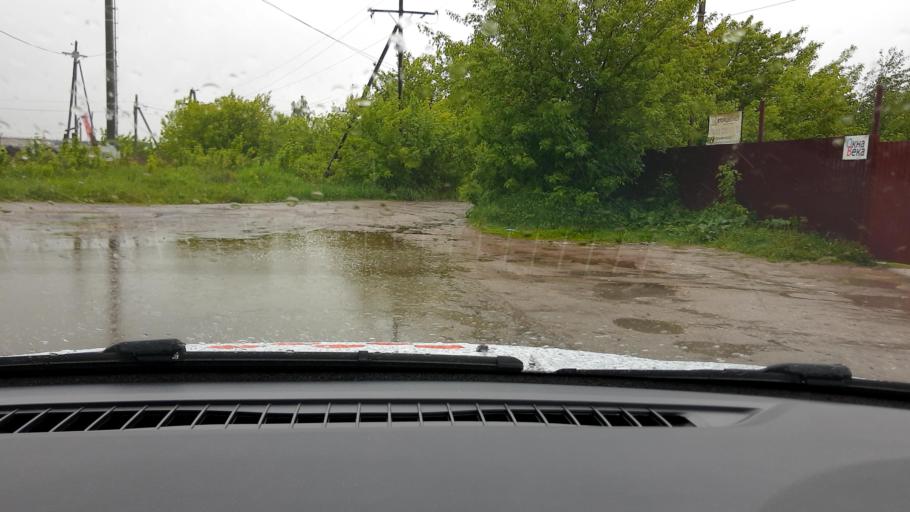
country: RU
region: Nizjnij Novgorod
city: Kstovo
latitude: 56.1387
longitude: 44.1887
